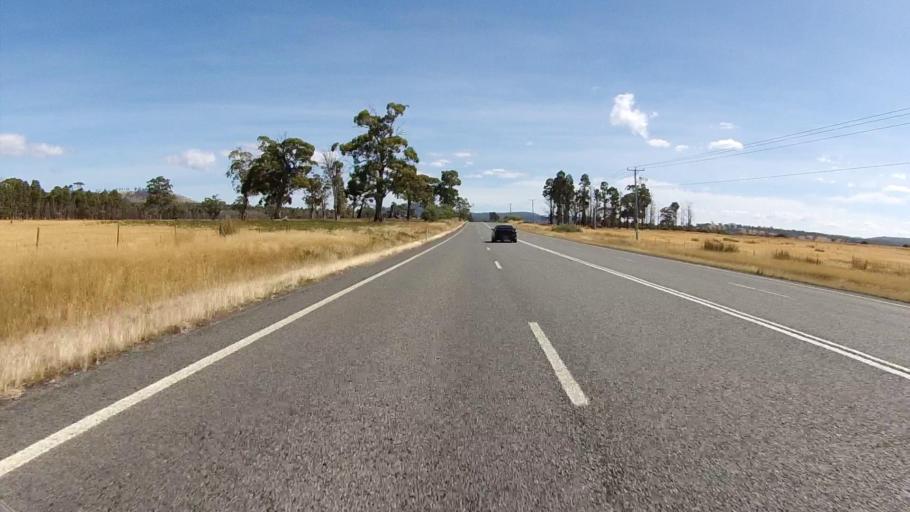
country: AU
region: Tasmania
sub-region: Sorell
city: Sorell
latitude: -42.6003
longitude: 147.7595
